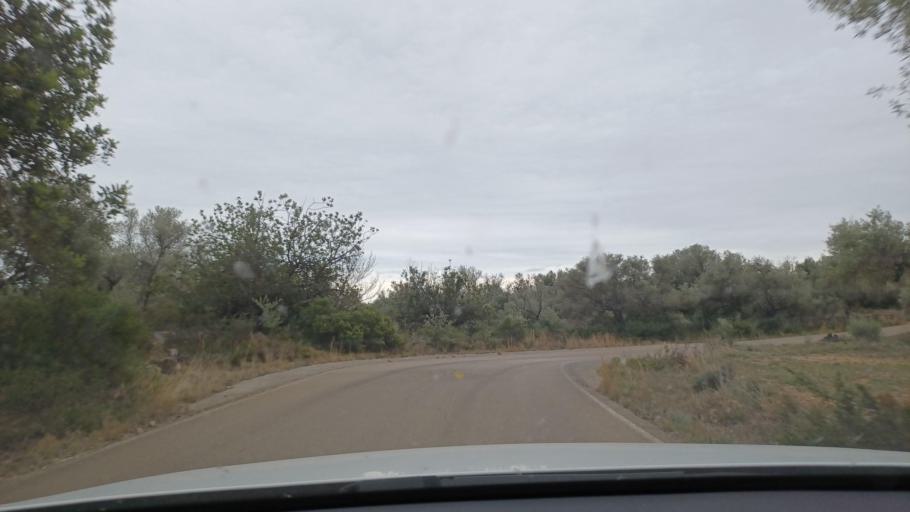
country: ES
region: Valencia
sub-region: Provincia de Castello
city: Canet lo Roig
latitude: 40.5941
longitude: 0.2840
